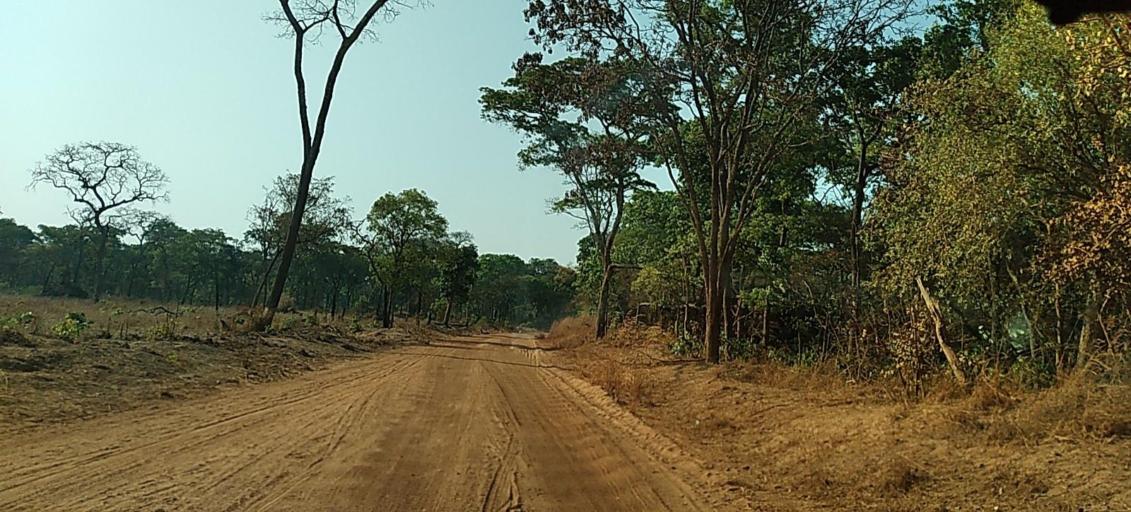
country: ZM
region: North-Western
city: Kasempa
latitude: -13.6503
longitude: 26.0040
